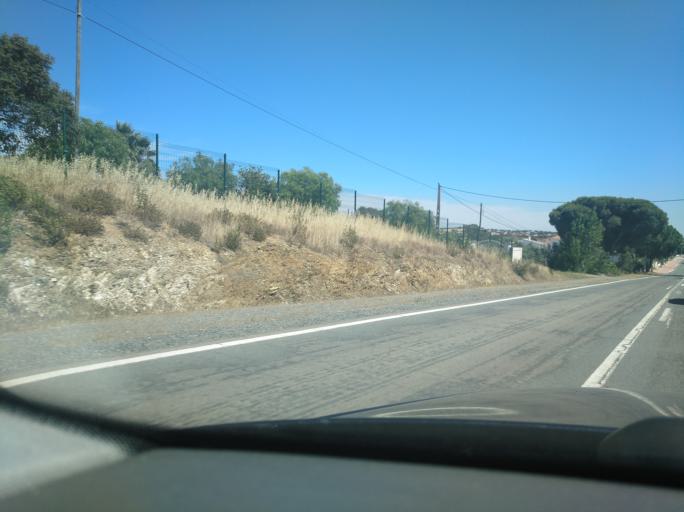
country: PT
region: Beja
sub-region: Castro Verde
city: Castro Verde
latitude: 37.6131
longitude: -8.0828
